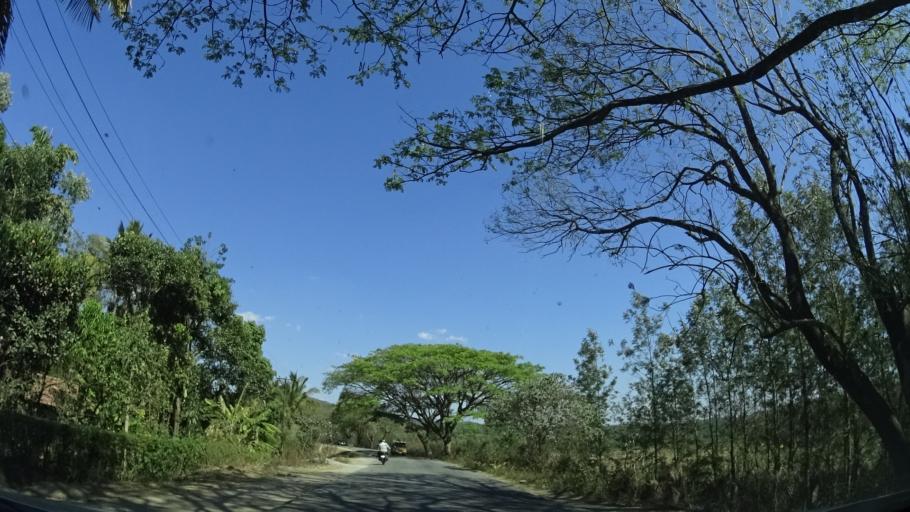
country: IN
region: Karnataka
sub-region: Chikmagalur
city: Chikmagalur
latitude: 13.2665
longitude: 75.7083
